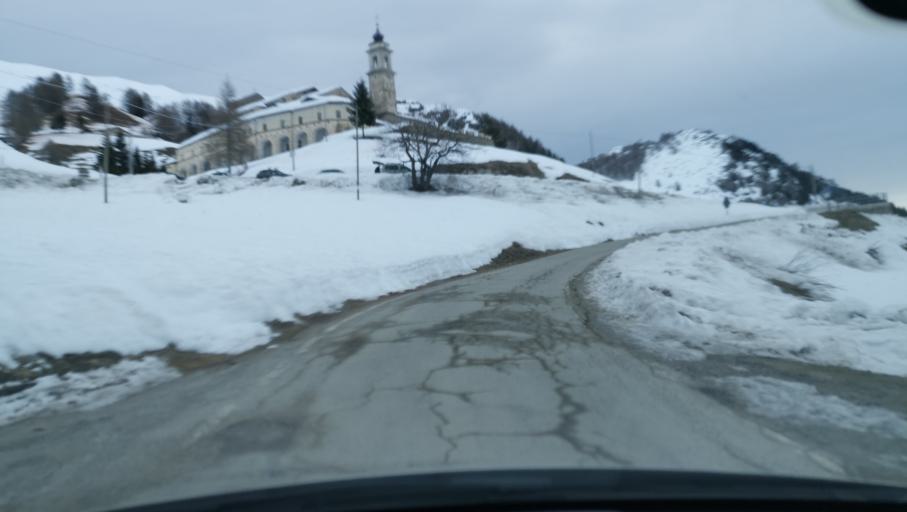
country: IT
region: Piedmont
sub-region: Provincia di Cuneo
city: Campomolino
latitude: 44.3997
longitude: 7.1696
